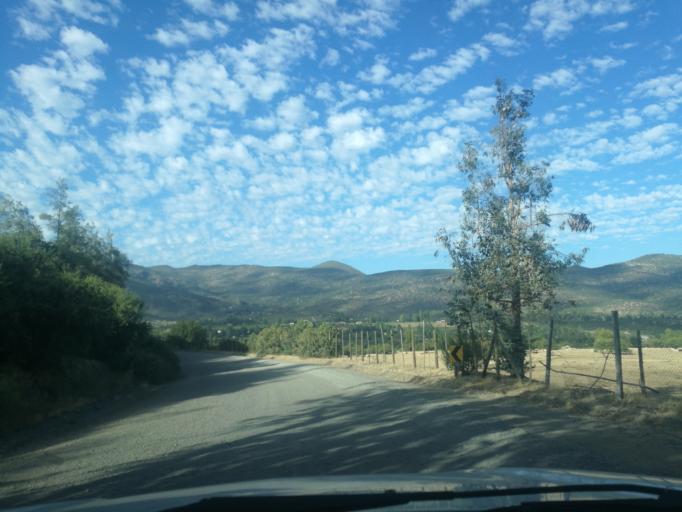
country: CL
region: O'Higgins
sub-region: Provincia de Cachapoal
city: Machali
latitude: -34.2363
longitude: -70.4738
